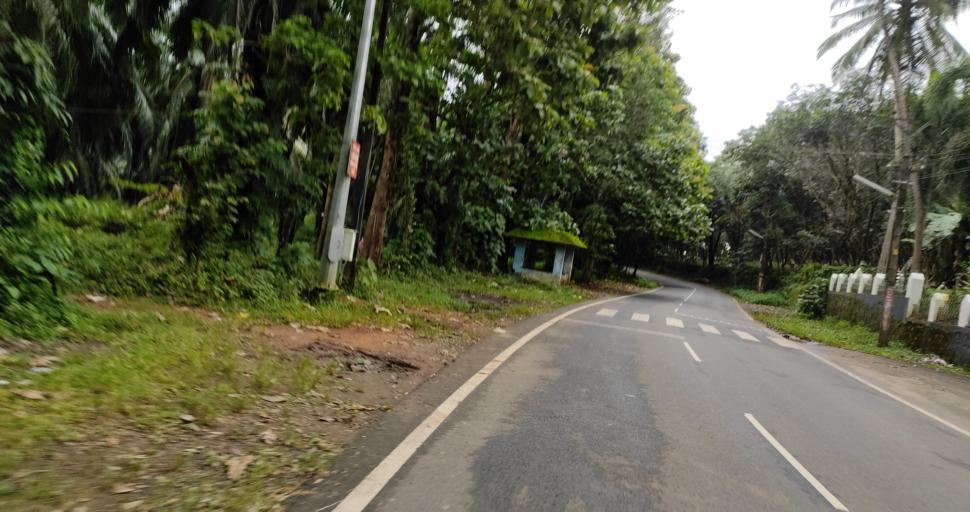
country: IN
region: Kerala
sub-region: Ernakulam
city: Angamali
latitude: 10.2955
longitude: 76.4855
